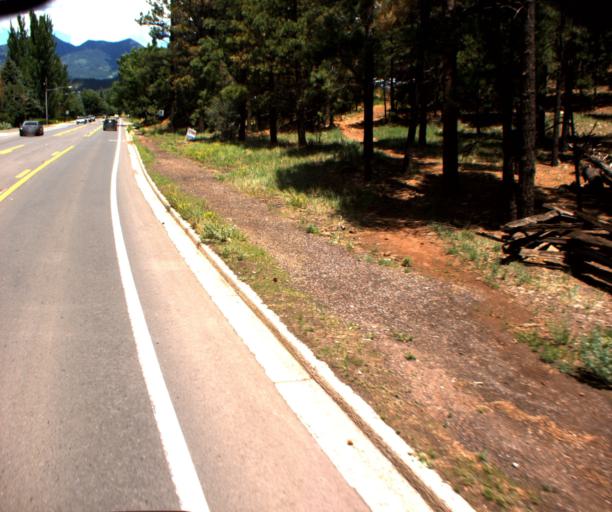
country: US
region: Arizona
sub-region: Coconino County
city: Flagstaff
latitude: 35.2125
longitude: -111.6501
